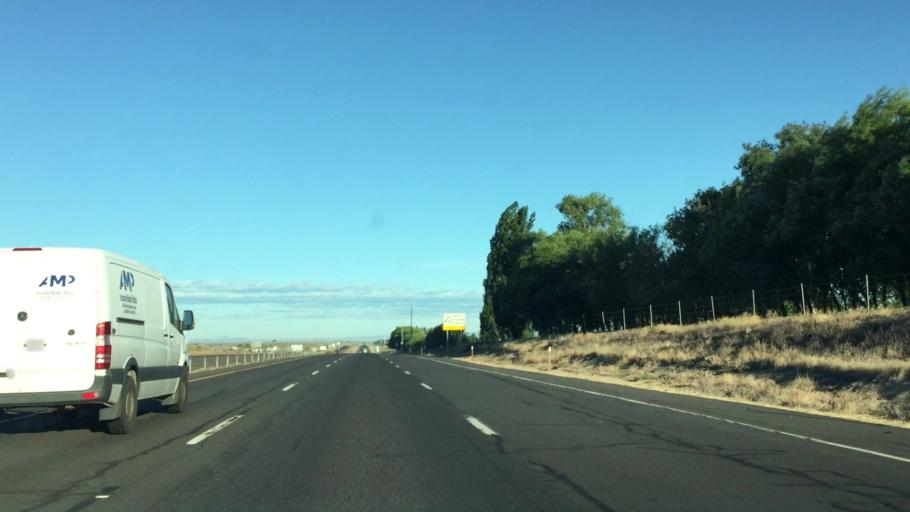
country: US
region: Washington
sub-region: Grant County
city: Cascade Valley
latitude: 47.1045
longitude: -119.3513
